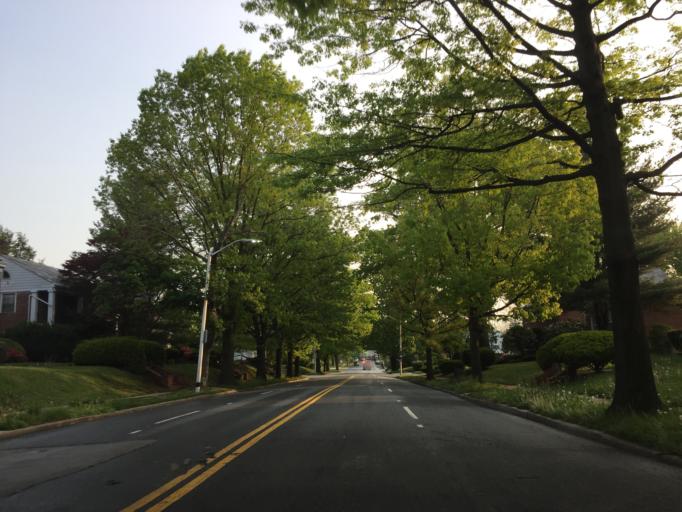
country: US
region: Maryland
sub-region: Baltimore County
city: Lochearn
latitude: 39.3272
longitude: -76.6699
